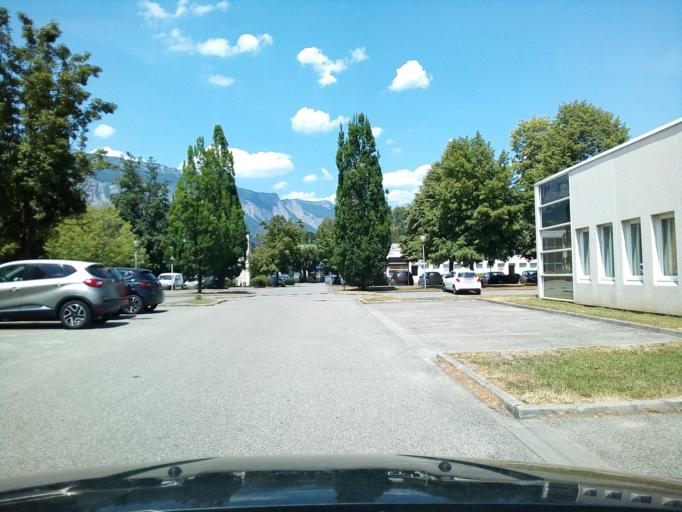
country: FR
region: Rhone-Alpes
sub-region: Departement de l'Isere
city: Gieres
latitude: 45.1902
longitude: 5.7794
